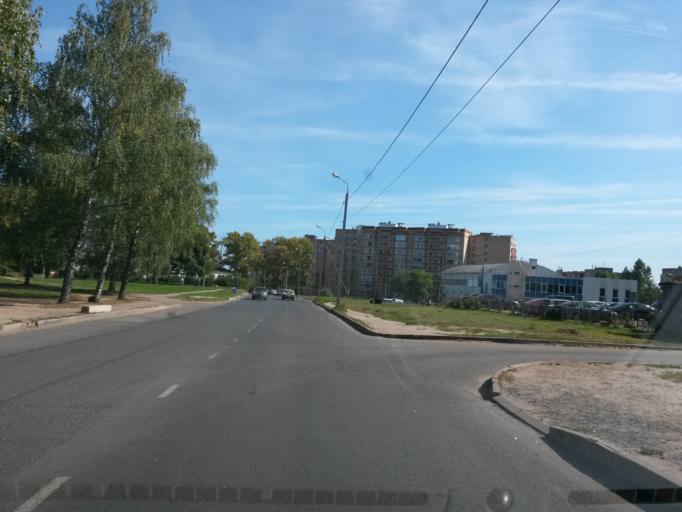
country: RU
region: Jaroslavl
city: Yaroslavl
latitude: 57.5792
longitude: 39.8594
